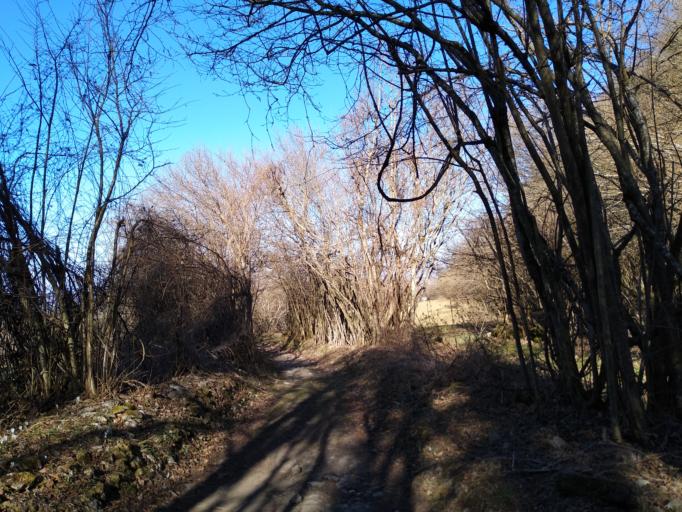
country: IT
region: Emilia-Romagna
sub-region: Provincia di Reggio Emilia
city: Castelnovo ne'Monti
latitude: 44.4258
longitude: 10.4143
